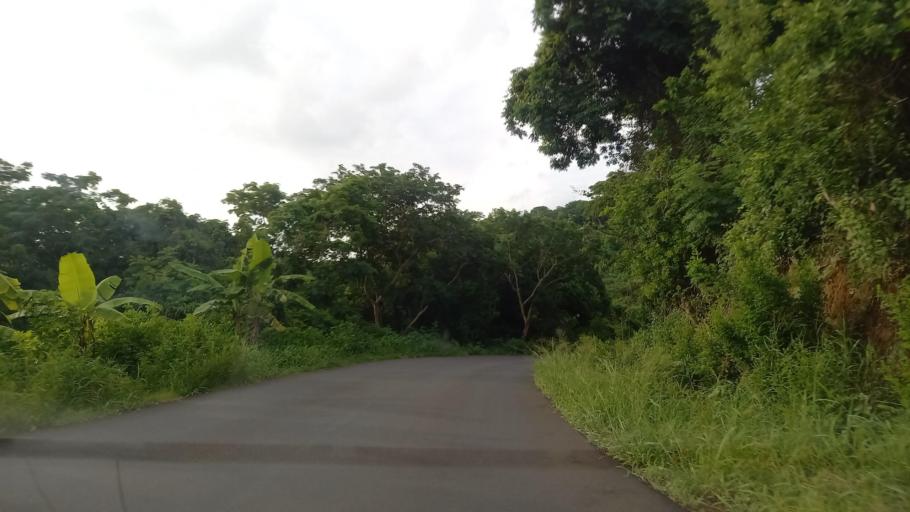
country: YT
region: M'Tsangamouji
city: M'Tsangamouji
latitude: -12.7503
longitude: 45.0642
